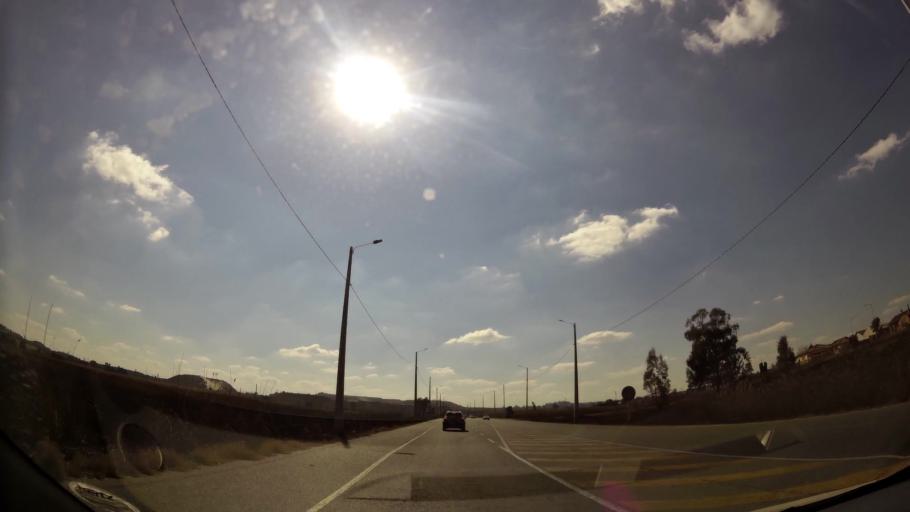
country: ZA
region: Gauteng
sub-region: West Rand District Municipality
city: Krugersdorp
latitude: -26.1514
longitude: 27.7630
